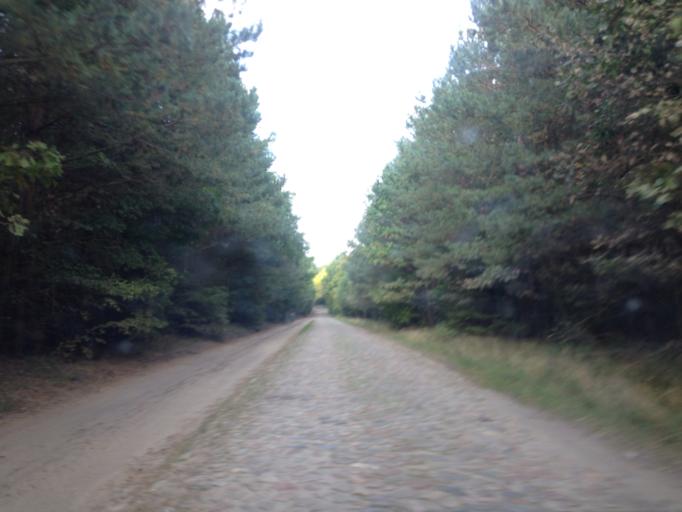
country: PL
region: Kujawsko-Pomorskie
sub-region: Powiat brodnicki
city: Gorzno
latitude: 53.2305
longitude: 19.6559
